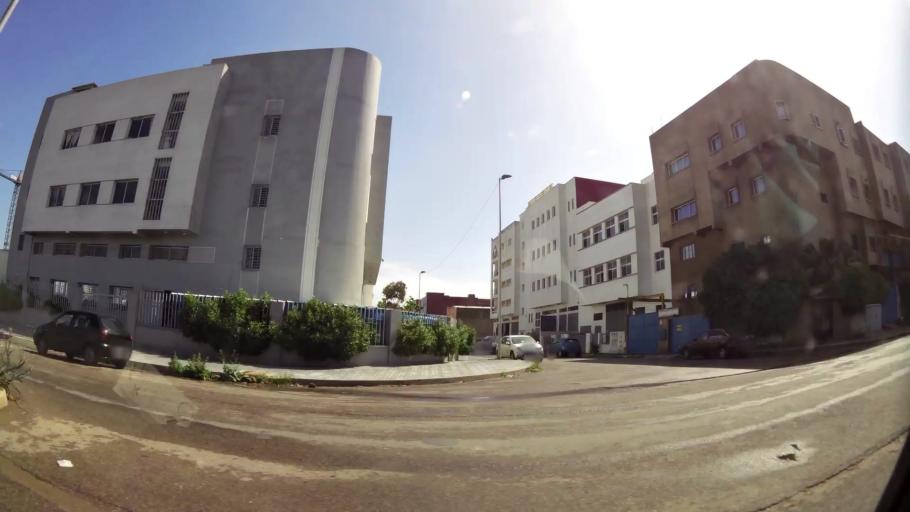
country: MA
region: Grand Casablanca
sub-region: Mediouna
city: Tit Mellil
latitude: 33.6184
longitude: -7.5090
